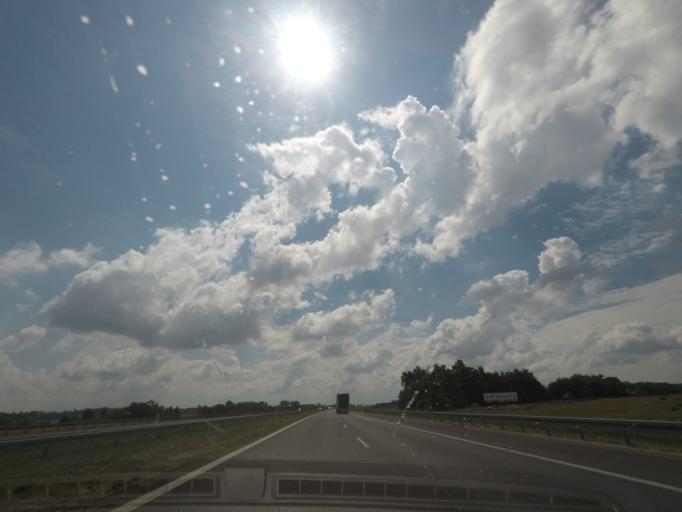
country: PL
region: Lodz Voivodeship
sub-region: Powiat zgierski
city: Strykow
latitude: 51.9448
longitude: 19.6085
